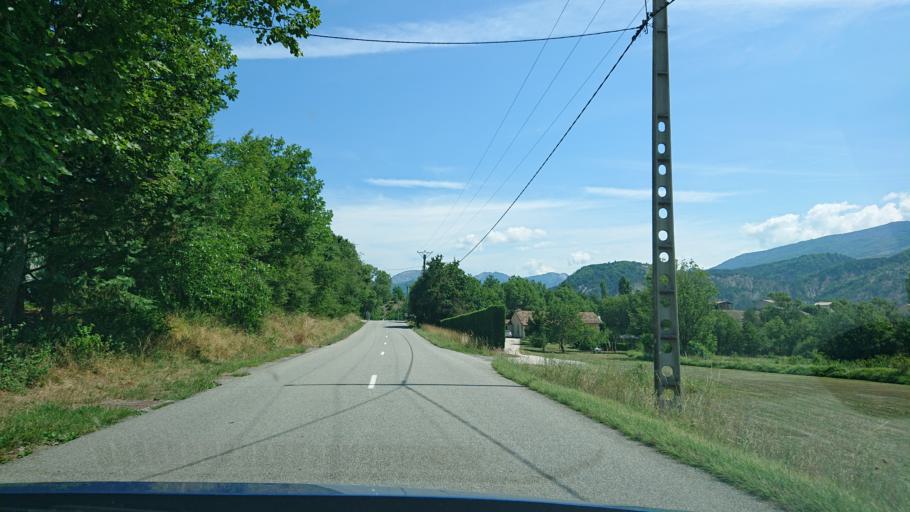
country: FR
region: Provence-Alpes-Cote d'Azur
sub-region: Departement des Alpes-de-Haute-Provence
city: Sisteron
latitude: 44.2805
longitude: 6.0135
